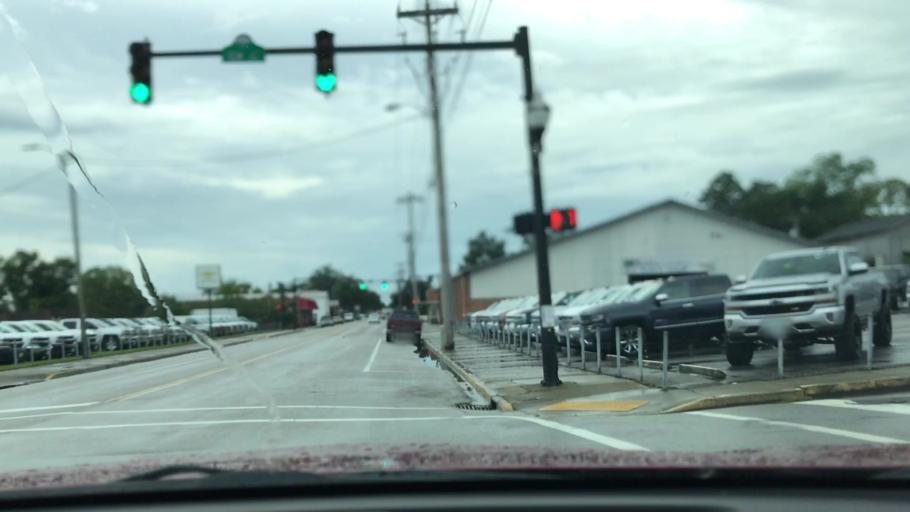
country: US
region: South Carolina
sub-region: Horry County
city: Conway
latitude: 33.8354
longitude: -79.0491
